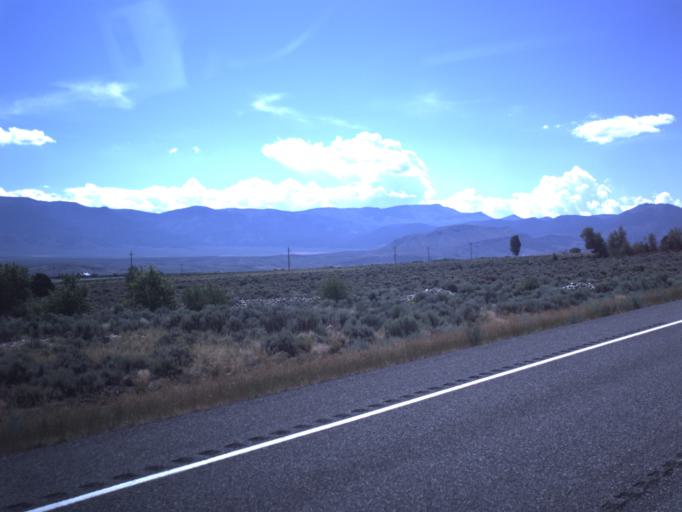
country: US
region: Utah
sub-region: Piute County
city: Junction
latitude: 38.3892
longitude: -112.2302
